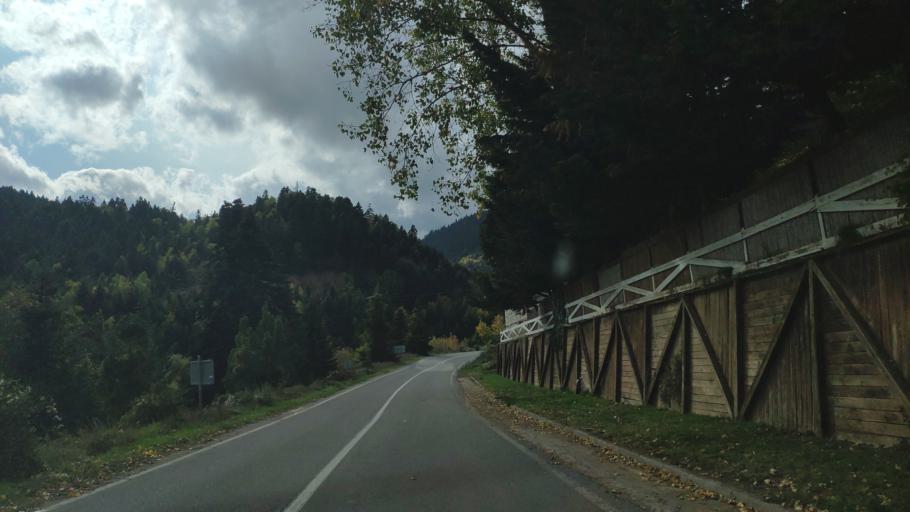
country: GR
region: Central Greece
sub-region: Nomos Fthiotidos
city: Stavros
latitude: 38.7326
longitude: 22.3465
